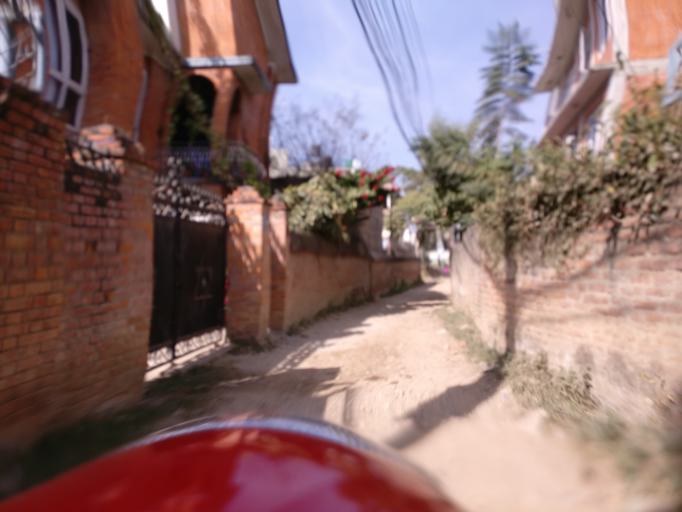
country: NP
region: Central Region
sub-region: Bagmati Zone
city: Patan
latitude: 27.6621
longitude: 85.3163
